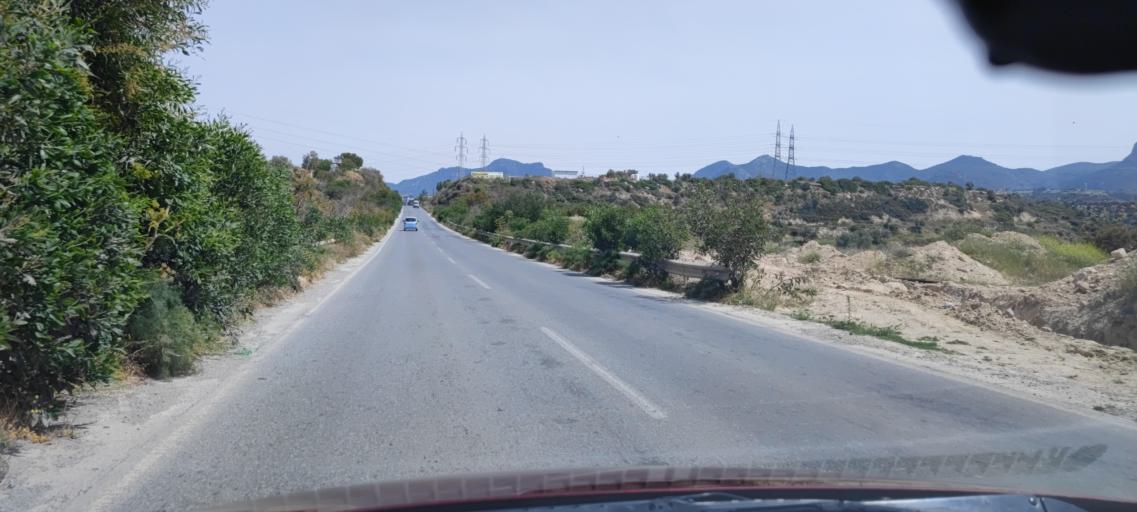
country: CY
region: Keryneia
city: Kyrenia
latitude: 35.3323
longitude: 33.4543
